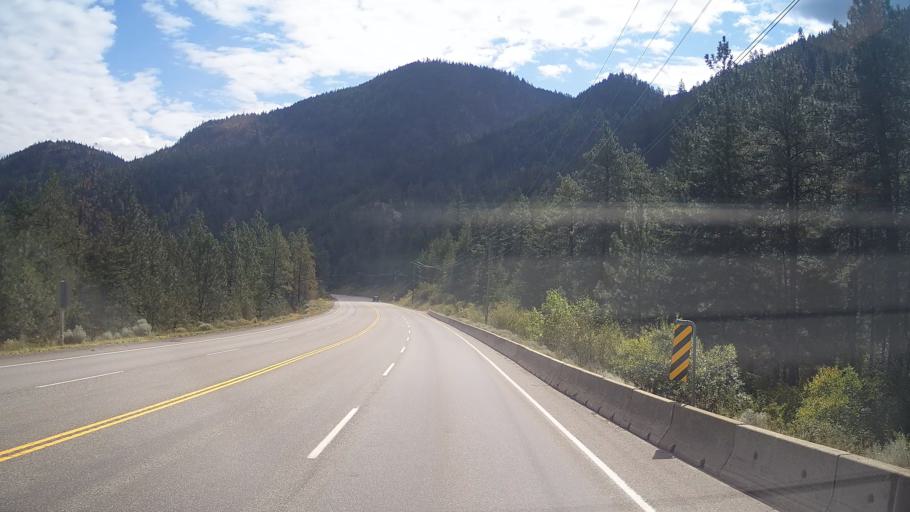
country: CA
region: British Columbia
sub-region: Thompson-Nicola Regional District
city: Ashcroft
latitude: 50.2463
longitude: -121.4930
